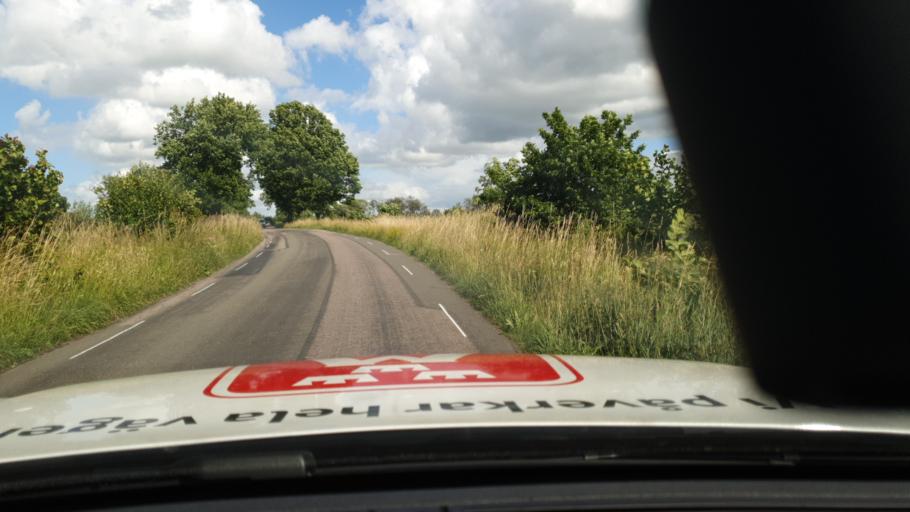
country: SE
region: Vaestra Goetaland
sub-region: Skovde Kommun
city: Stopen
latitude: 58.4935
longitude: 13.7861
